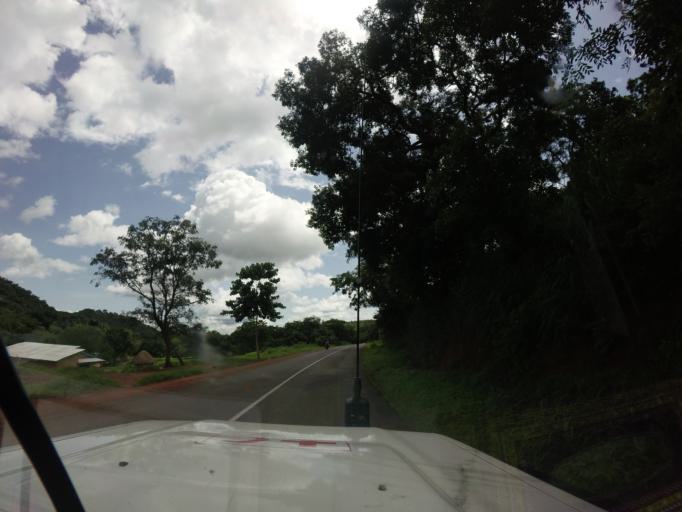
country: SL
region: Northern Province
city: Bindi
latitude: 10.1374
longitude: -11.6395
